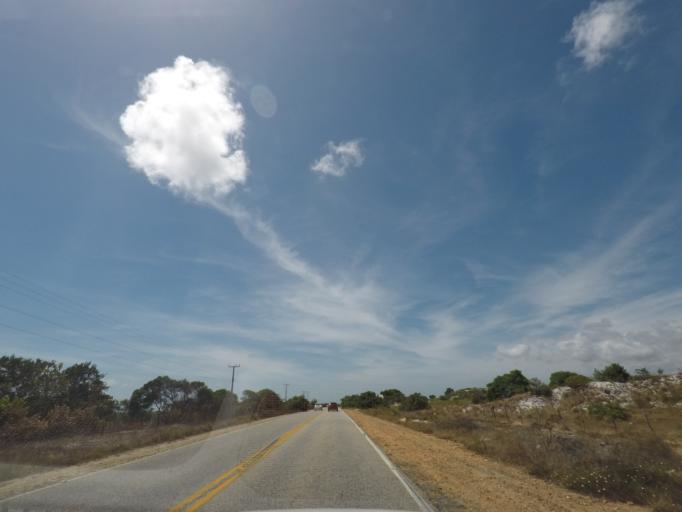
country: BR
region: Sergipe
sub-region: Sao Cristovao
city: Sao Cristovao
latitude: -11.1315
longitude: -37.1868
